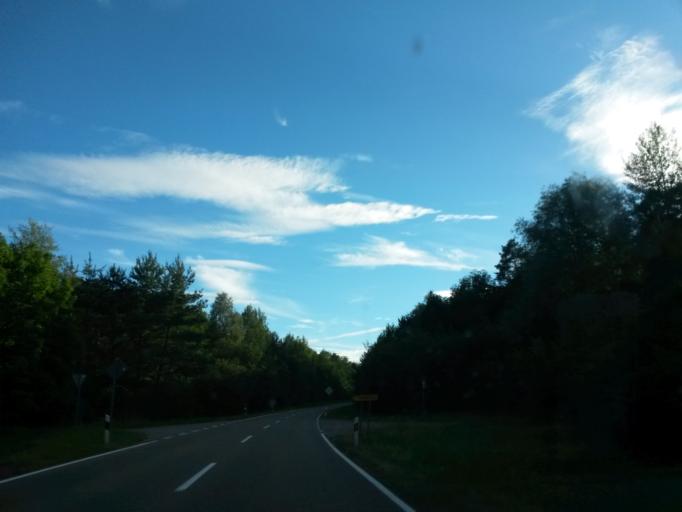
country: DE
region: Baden-Wuerttemberg
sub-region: Regierungsbezirk Stuttgart
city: Ellenberg
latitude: 48.9882
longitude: 10.2023
